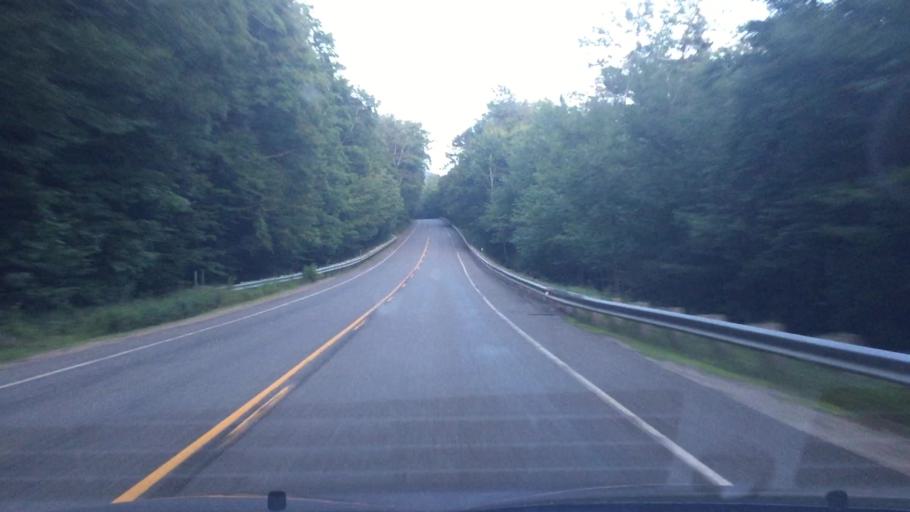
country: US
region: New Hampshire
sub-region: Grafton County
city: Woodstock
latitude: 44.0496
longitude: -71.5648
